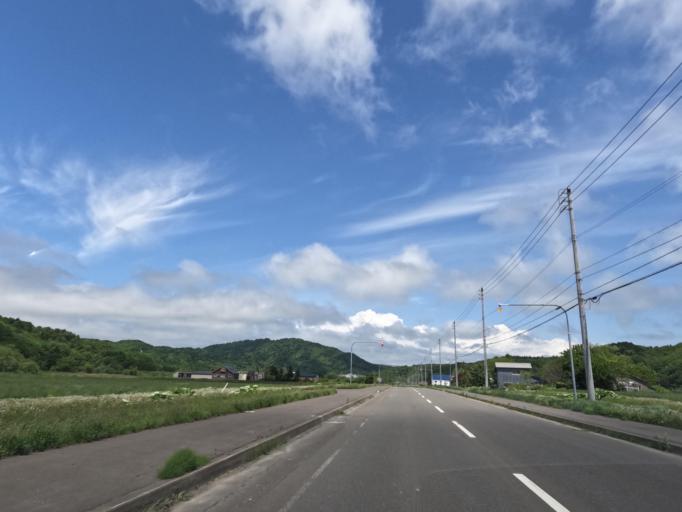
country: JP
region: Hokkaido
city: Tobetsu
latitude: 43.3011
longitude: 141.5492
